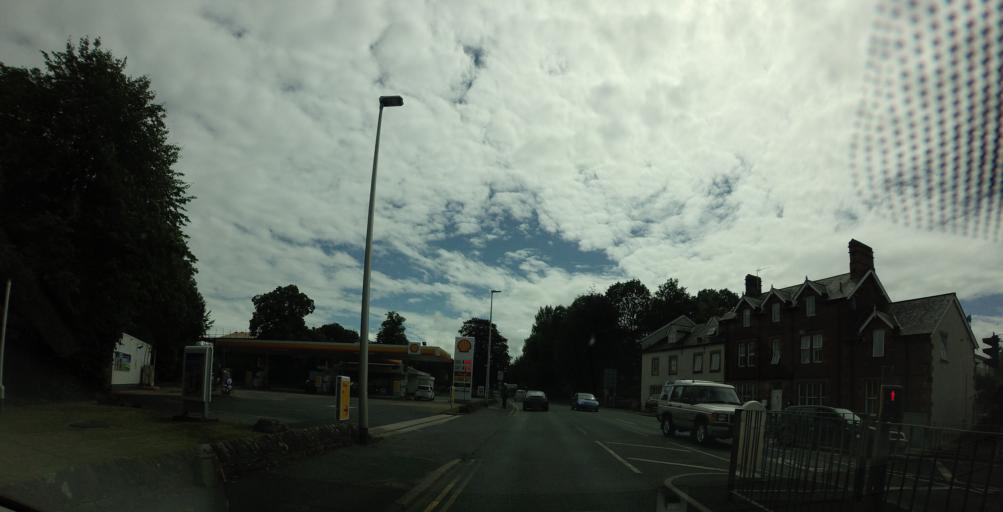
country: GB
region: England
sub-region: Cumbria
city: Penrith
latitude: 54.6603
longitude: -2.7478
